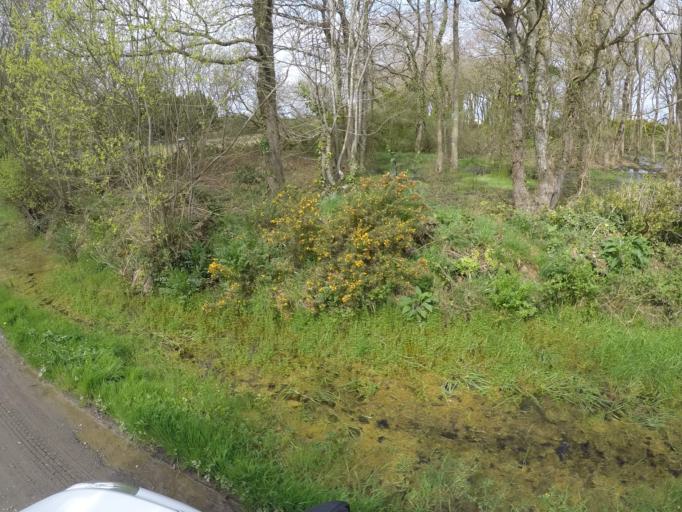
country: FR
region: Brittany
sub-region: Departement des Cotes-d'Armor
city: Plouezec
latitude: 48.7187
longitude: -2.9566
